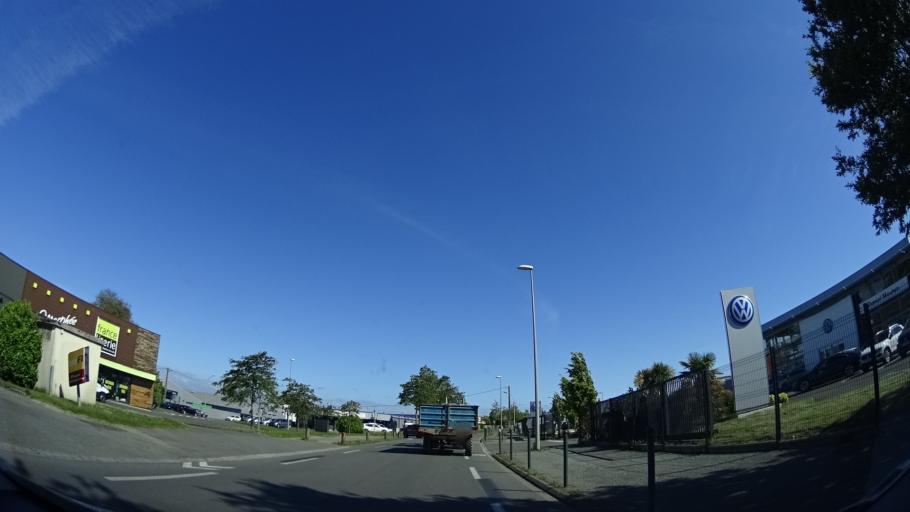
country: FR
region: Brittany
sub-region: Departement d'Ille-et-Vilaine
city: Saint-Jouan-des-Guerets
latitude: 48.6217
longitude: -1.9867
